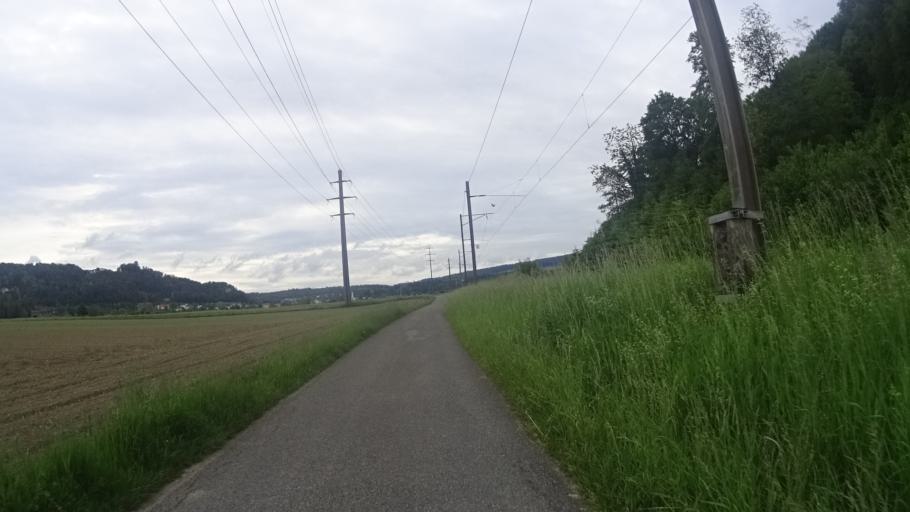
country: DE
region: Baden-Wuerttemberg
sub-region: Freiburg Region
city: Waldshut-Tiengen
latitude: 47.6113
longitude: 8.2119
